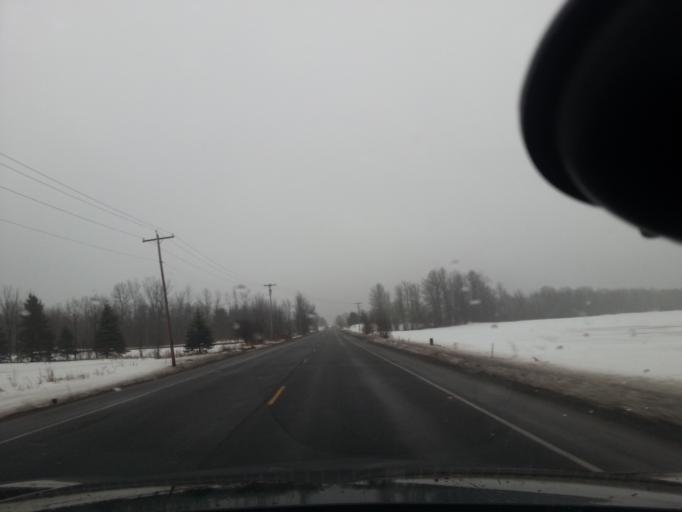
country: US
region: New York
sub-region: St. Lawrence County
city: Ogdensburg
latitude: 44.6055
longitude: -75.3925
